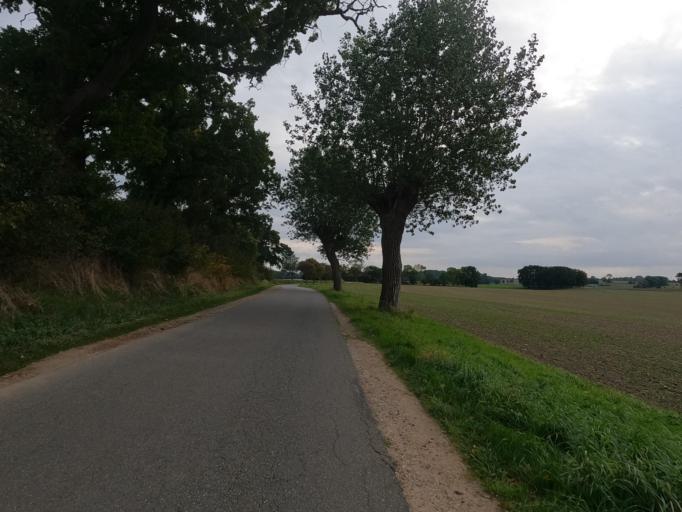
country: DE
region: Schleswig-Holstein
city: Heringsdorf
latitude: 54.2817
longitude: 11.0536
